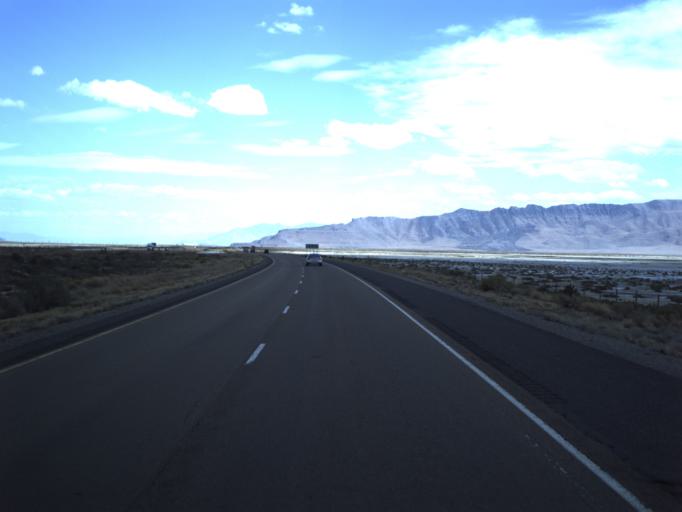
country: US
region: Utah
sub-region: Tooele County
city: Grantsville
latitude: 40.7574
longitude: -112.7685
